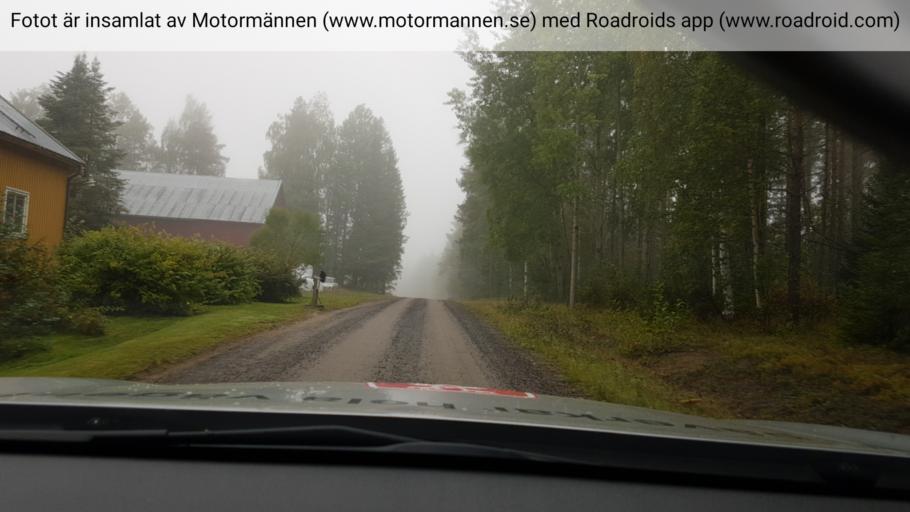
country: SE
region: Vaesterbotten
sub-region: Skelleftea Kommun
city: Burtraesk
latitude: 64.2562
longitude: 20.5759
